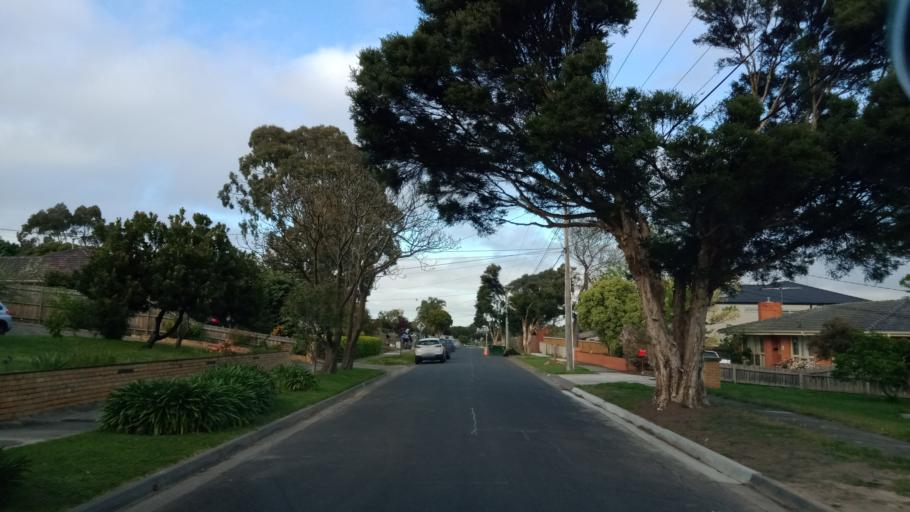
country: AU
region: Victoria
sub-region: Monash
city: Notting Hill
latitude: -37.8881
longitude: 145.1379
